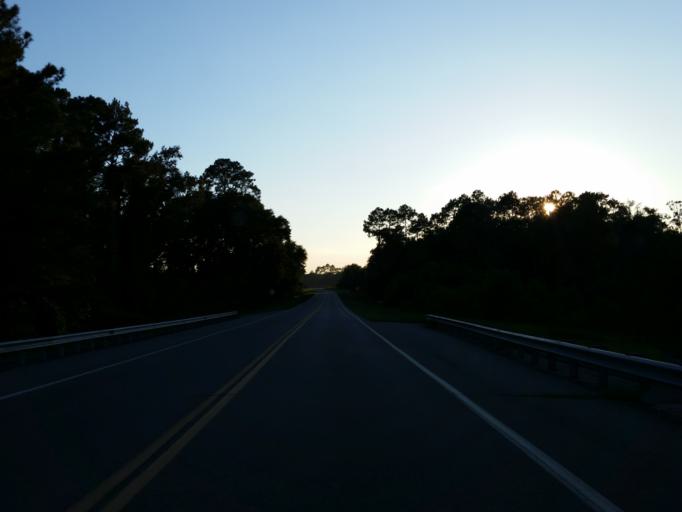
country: US
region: Georgia
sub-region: Berrien County
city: Nashville
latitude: 31.1862
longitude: -83.1800
